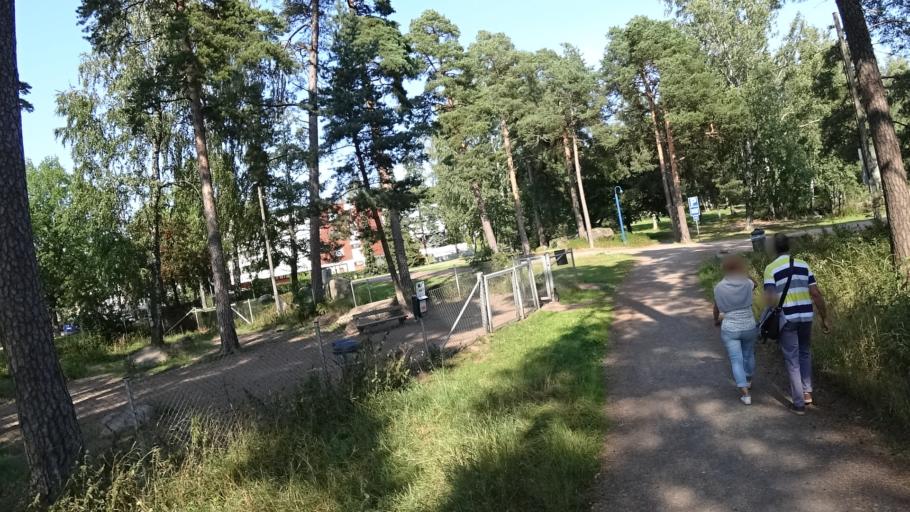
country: FI
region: Kymenlaakso
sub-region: Kotka-Hamina
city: Kotka
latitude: 60.4521
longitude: 26.9482
